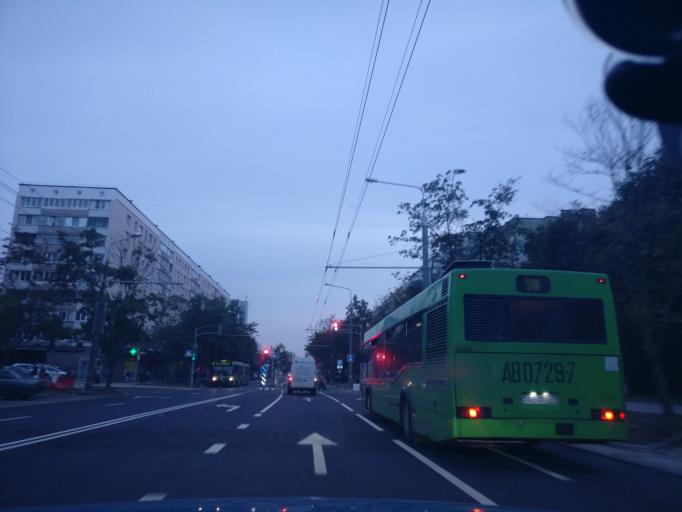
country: BY
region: Minsk
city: Minsk
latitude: 53.9246
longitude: 27.5811
